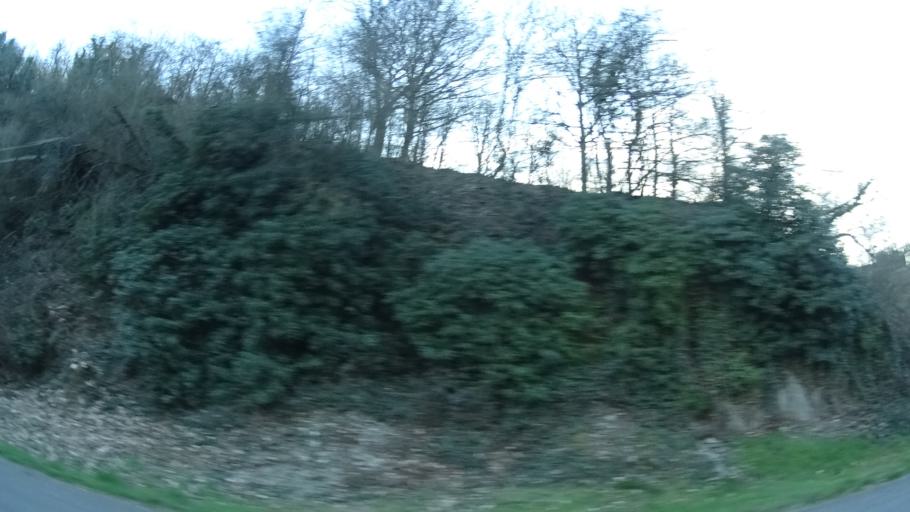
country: DE
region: Rheinland-Pfalz
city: Bingen am Rhein
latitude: 49.9599
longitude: 7.8916
